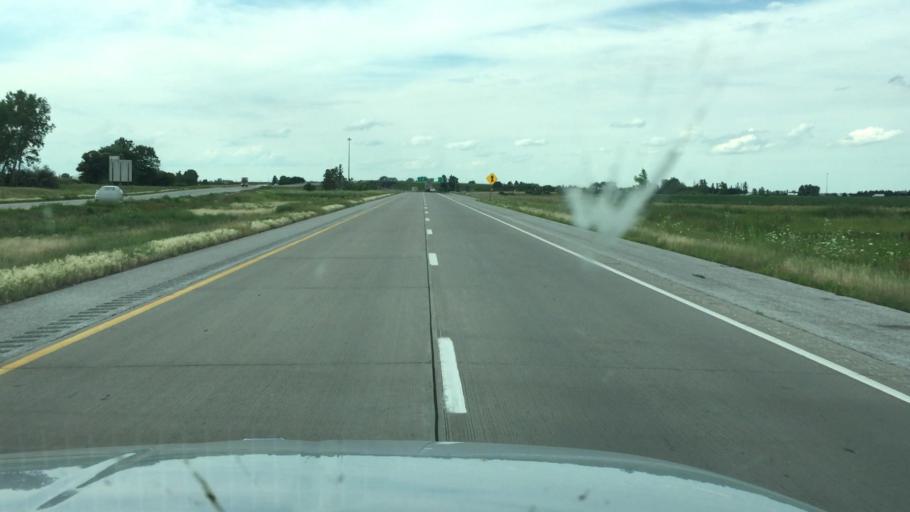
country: US
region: Iowa
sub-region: Scott County
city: Walcott
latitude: 41.5932
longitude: -90.6757
